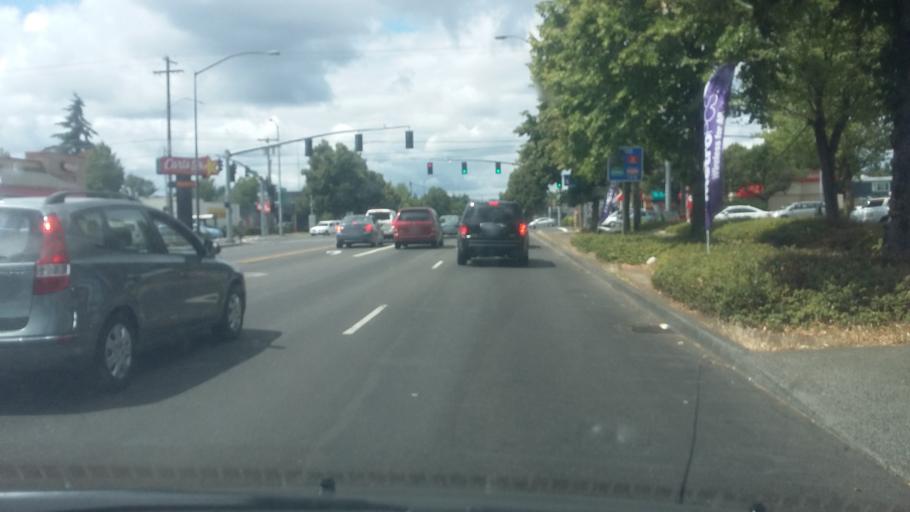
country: US
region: Oregon
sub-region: Multnomah County
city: Lents
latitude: 45.4975
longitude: -122.5777
